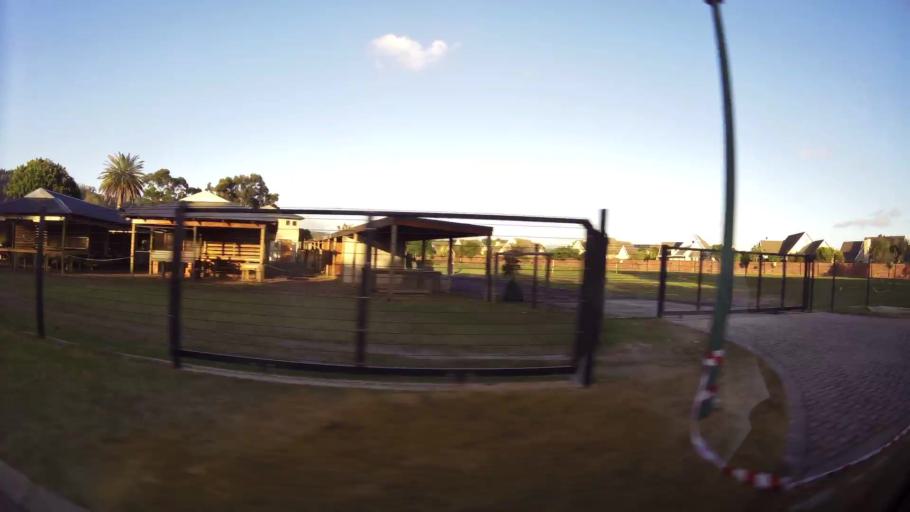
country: ZA
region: Western Cape
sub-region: Eden District Municipality
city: Knysna
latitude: -34.0105
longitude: 22.7793
